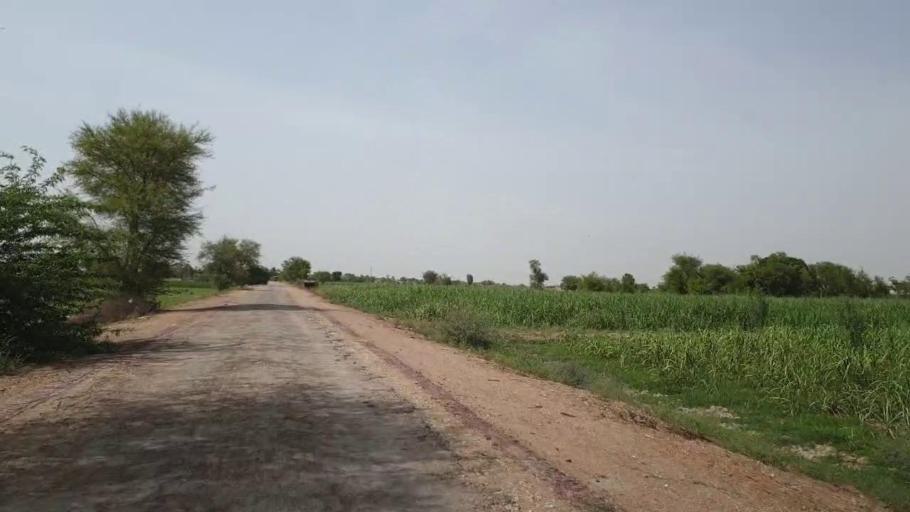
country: PK
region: Sindh
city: Daur
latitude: 26.5346
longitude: 68.4076
